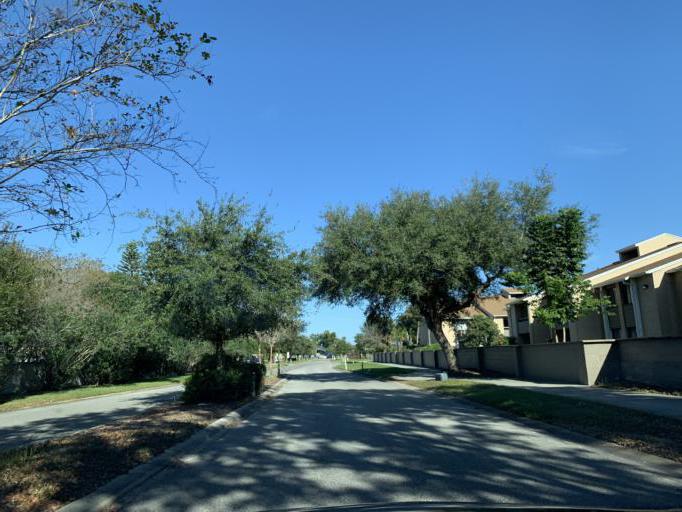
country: US
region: Florida
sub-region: Orange County
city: Oak Ridge
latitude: 28.4835
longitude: -81.4478
